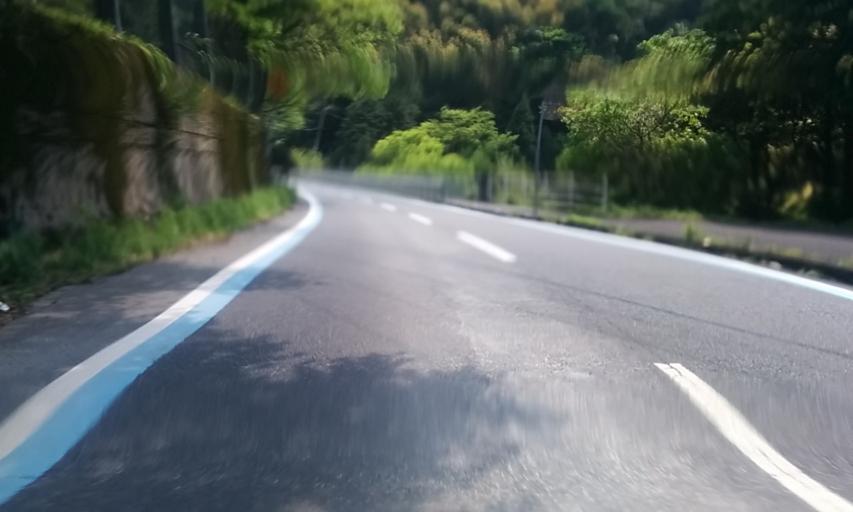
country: JP
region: Ehime
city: Saijo
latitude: 33.8556
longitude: 133.1978
